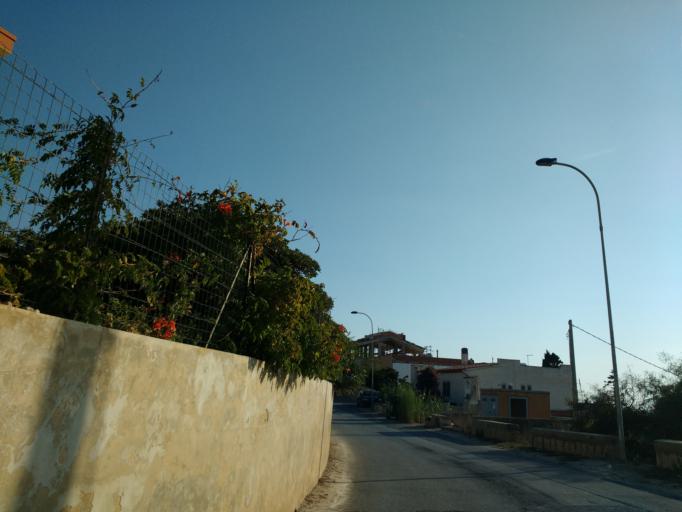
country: IT
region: Sicily
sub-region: Ragusa
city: Cava d'Aliga
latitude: 36.7290
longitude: 14.6908
